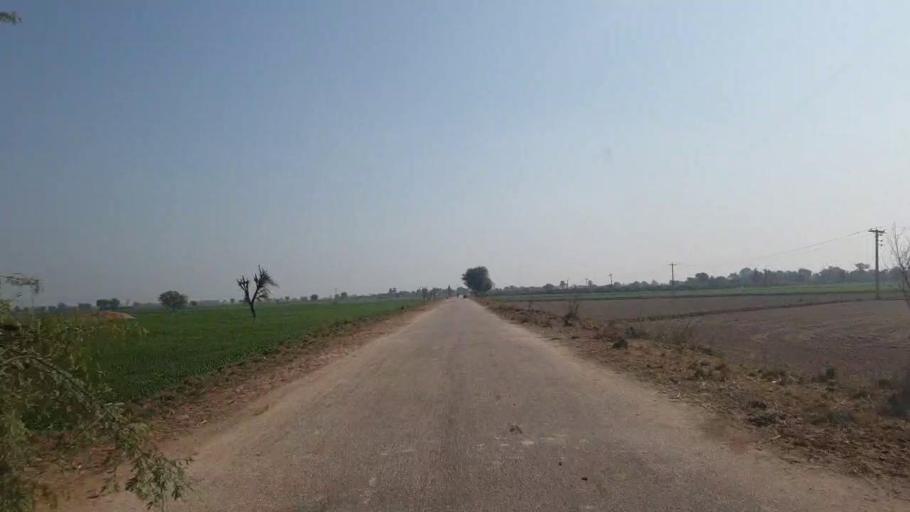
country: PK
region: Sindh
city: Sakrand
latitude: 26.0425
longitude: 68.4254
